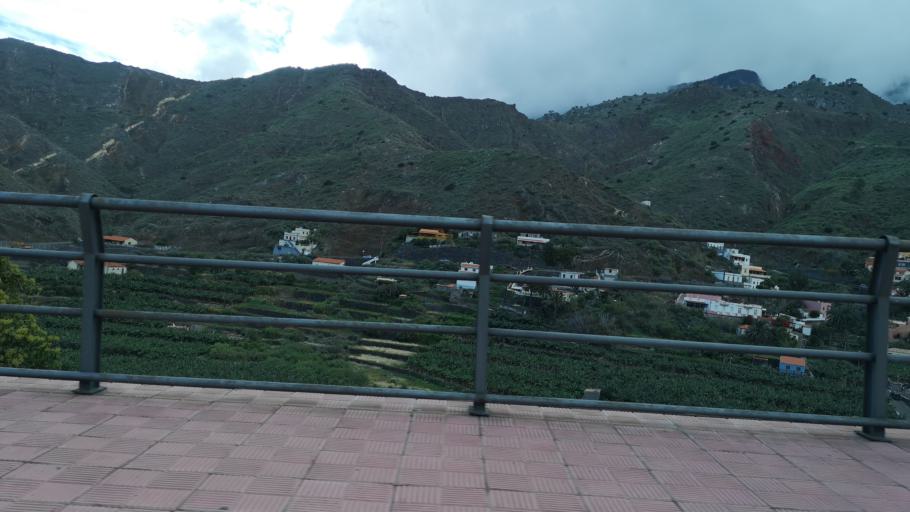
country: ES
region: Canary Islands
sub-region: Provincia de Santa Cruz de Tenerife
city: Hermigua
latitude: 28.1736
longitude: -17.1874
